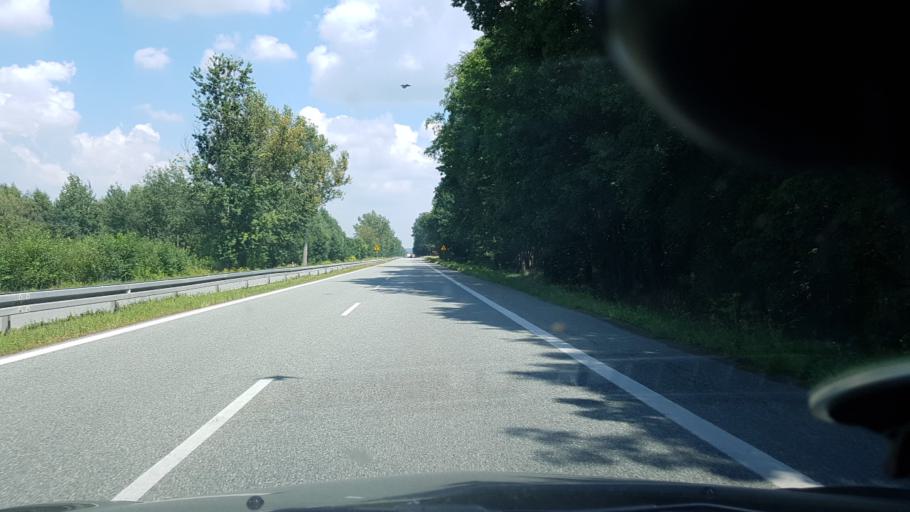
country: PL
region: Silesian Voivodeship
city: Gardawice
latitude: 50.0936
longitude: 18.7670
